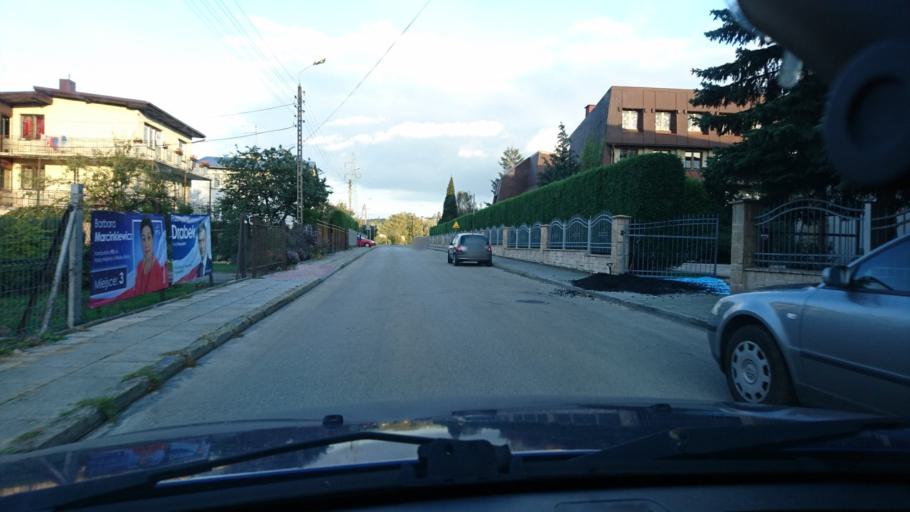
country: PL
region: Silesian Voivodeship
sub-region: Bielsko-Biala
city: Bielsko-Biala
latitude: 49.8424
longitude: 19.0629
